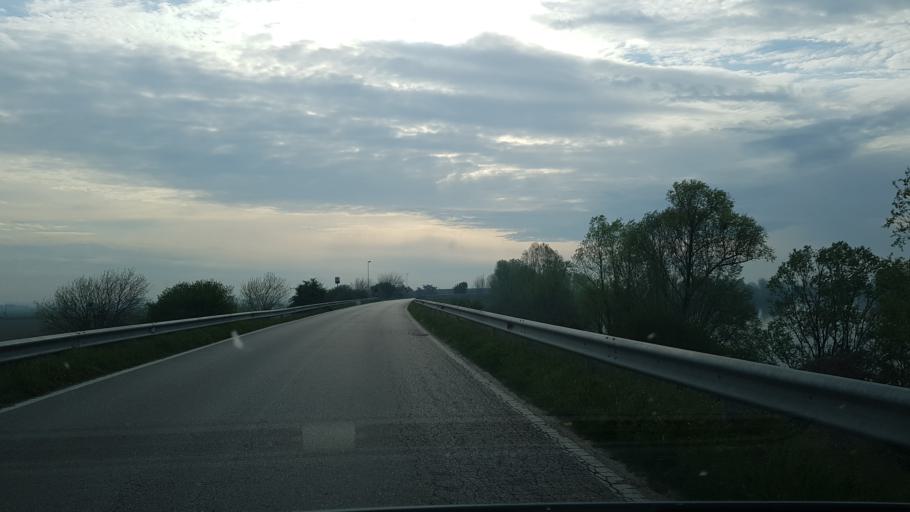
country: IT
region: Veneto
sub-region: Provincia di Rovigo
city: Lendinara
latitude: 45.1191
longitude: 11.5970
